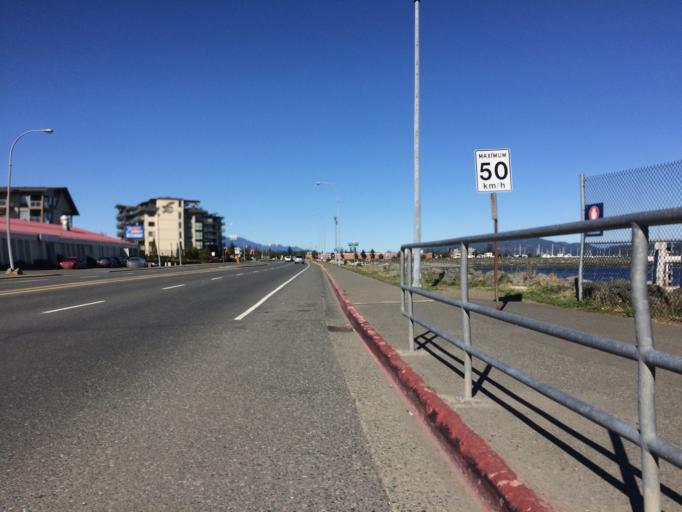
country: CA
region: British Columbia
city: Campbell River
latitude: 50.0281
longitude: -125.2427
